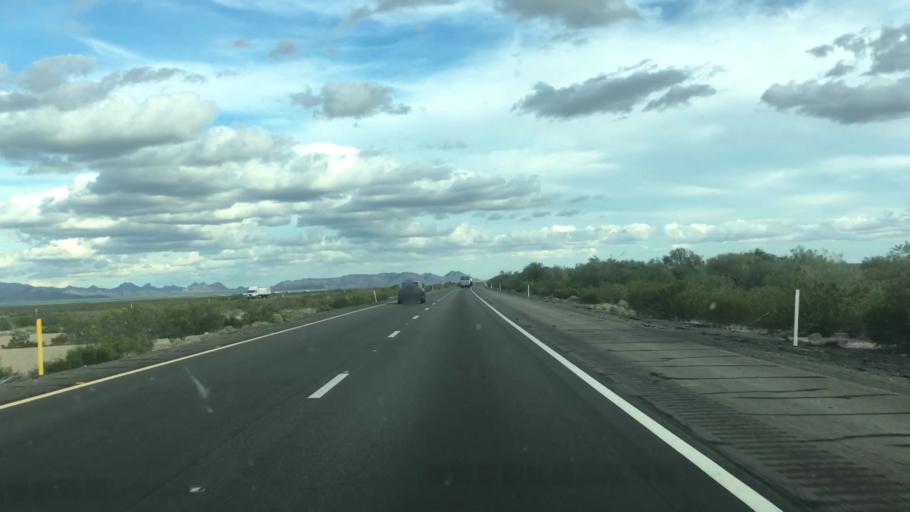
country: US
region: Arizona
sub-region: La Paz County
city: Salome
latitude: 33.6382
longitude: -113.8225
